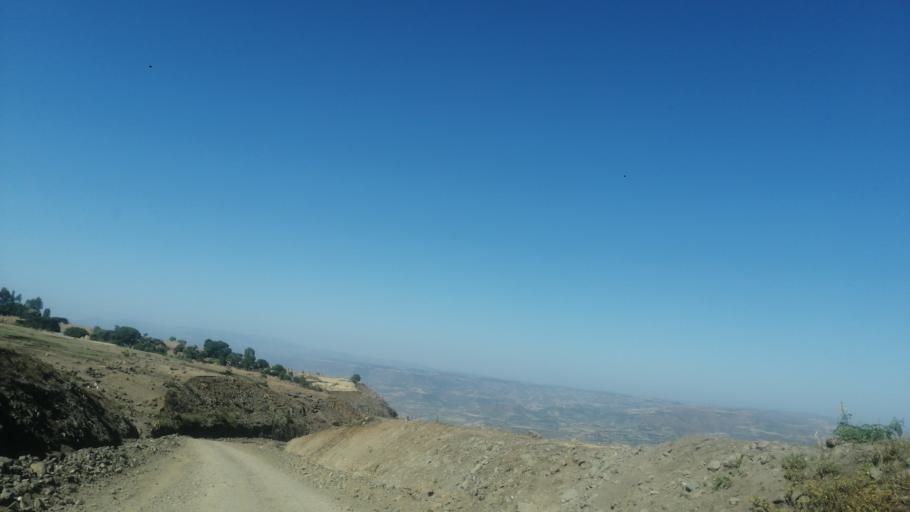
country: ET
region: Amhara
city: Addiet Canna
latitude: 11.1520
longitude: 37.8621
